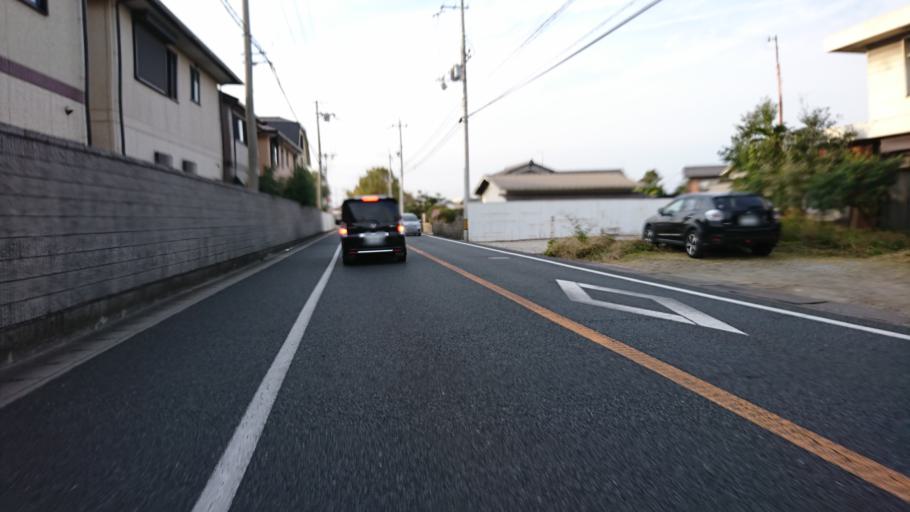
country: JP
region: Hyogo
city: Kakogawacho-honmachi
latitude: 34.7297
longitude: 134.8389
